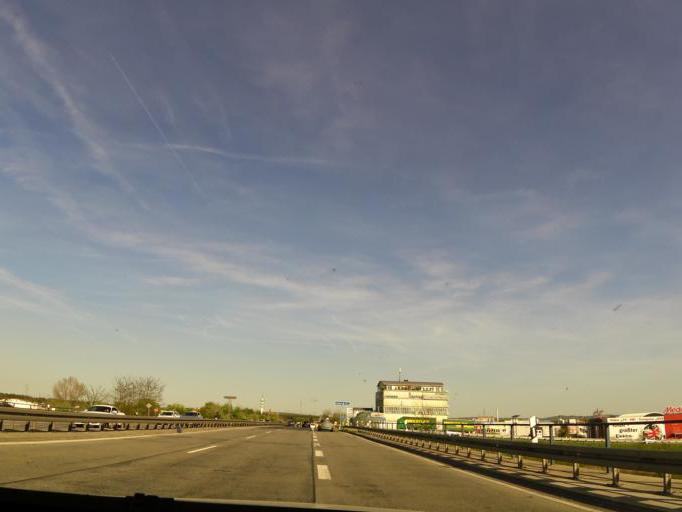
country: DE
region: Hesse
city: Weiterstadt
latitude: 49.8985
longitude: 8.6058
